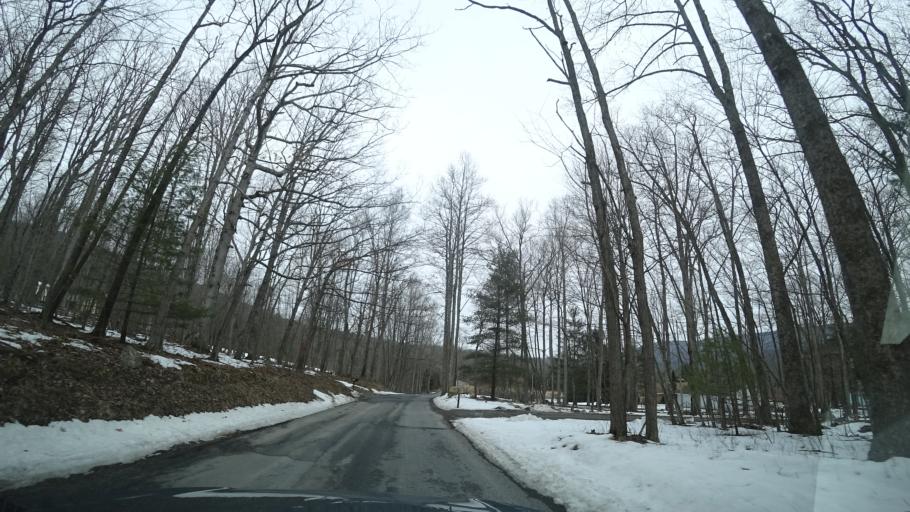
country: US
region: Virginia
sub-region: Shenandoah County
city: Basye
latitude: 38.9447
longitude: -78.6924
